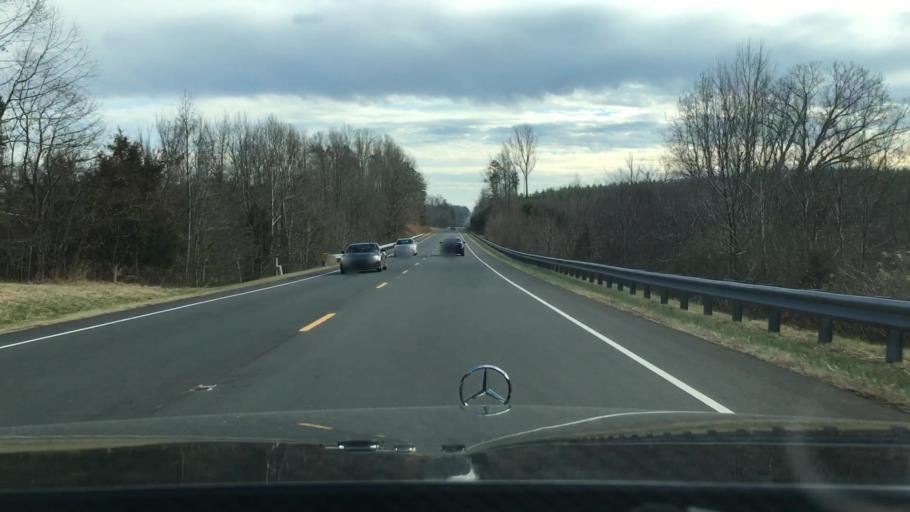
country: US
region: Virginia
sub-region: City of Danville
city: Danville
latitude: 36.5183
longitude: -79.3941
